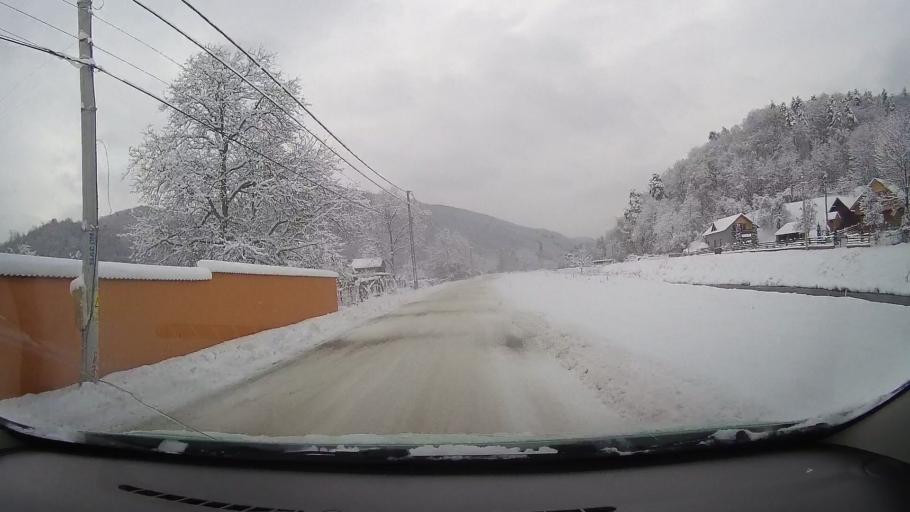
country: RO
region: Alba
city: Pianu de Sus
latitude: 45.8883
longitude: 23.4876
